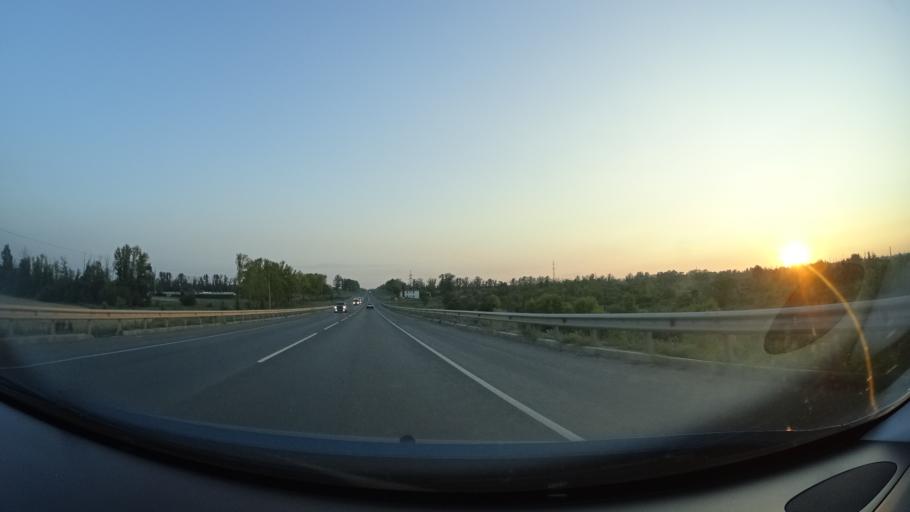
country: RU
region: Samara
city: Sukhodol
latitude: 53.8852
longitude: 51.2437
